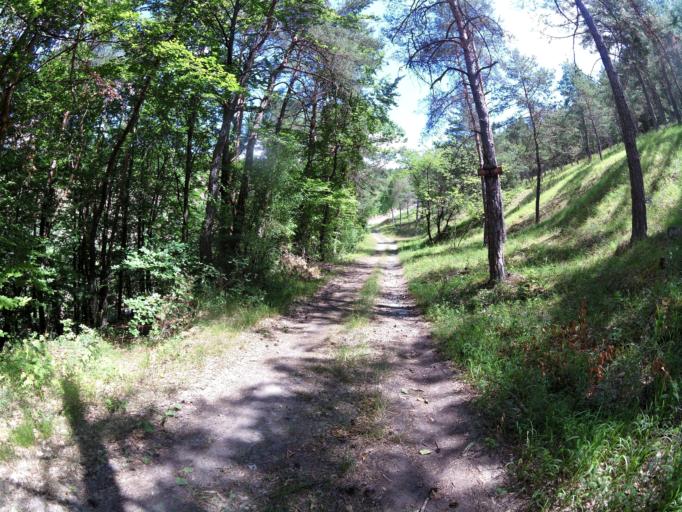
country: DE
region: Bavaria
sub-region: Regierungsbezirk Unterfranken
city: Thungersheim
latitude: 49.8924
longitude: 9.8440
